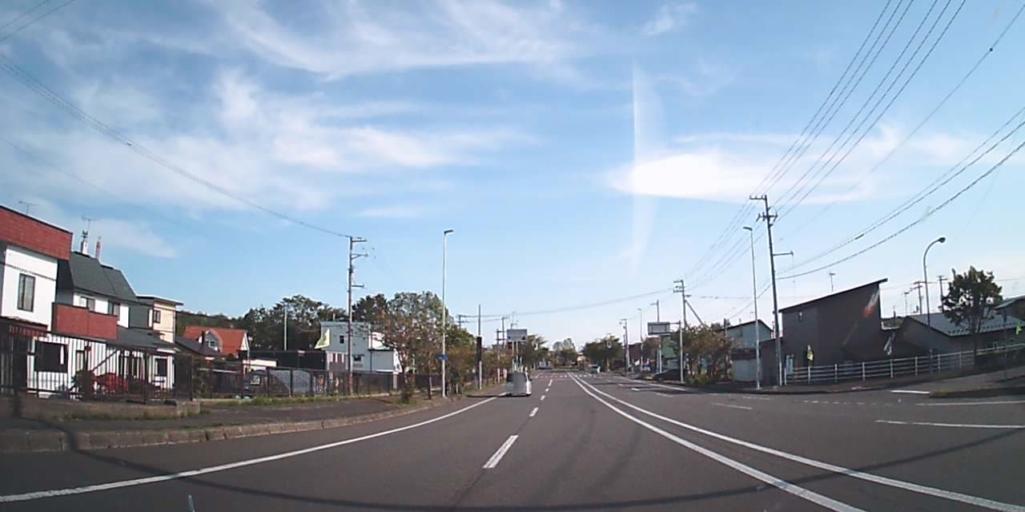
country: JP
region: Hokkaido
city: Shiraoi
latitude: 42.4580
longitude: 141.1774
